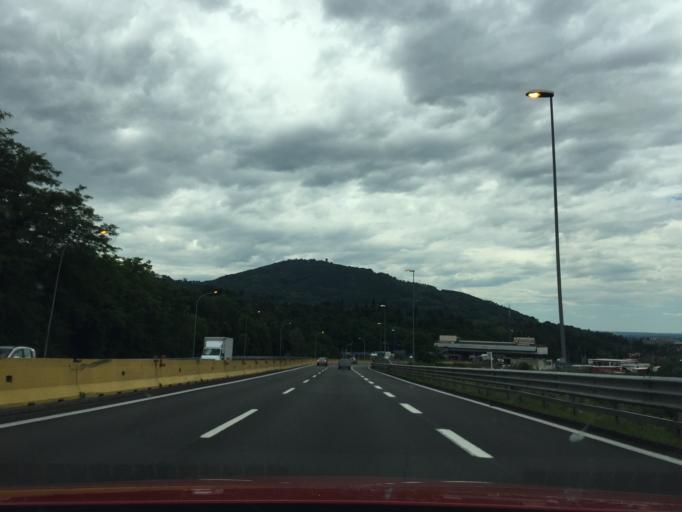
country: IT
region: Tuscany
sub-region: Provincia di Pistoia
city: Serravalle Pistoiese
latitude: 43.8946
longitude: 10.8265
